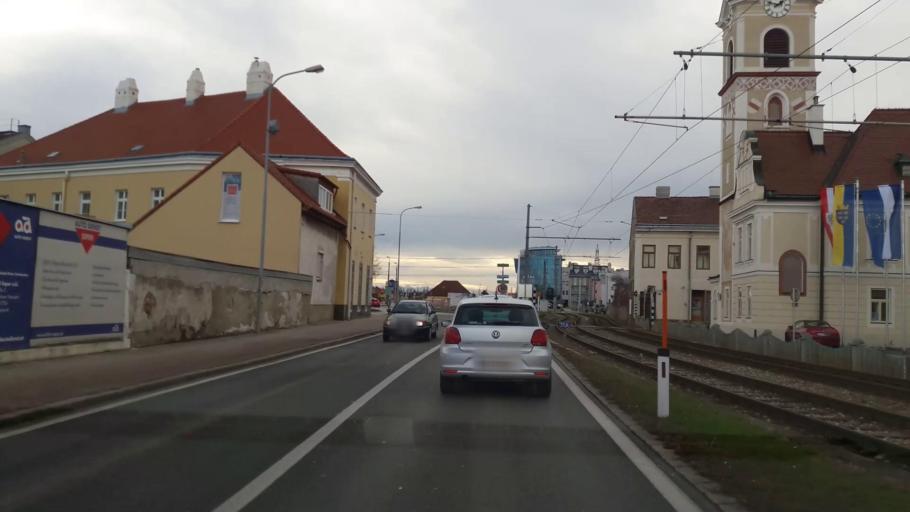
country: AT
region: Lower Austria
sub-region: Politischer Bezirk Modling
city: Wiener Neudorf
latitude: 48.0837
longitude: 16.3140
